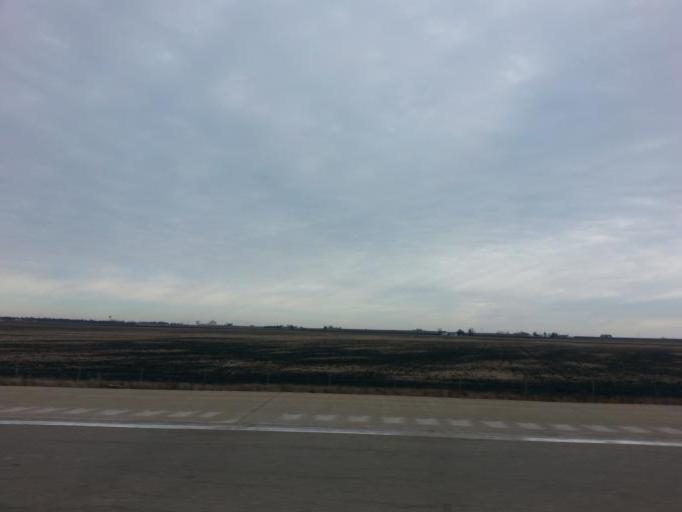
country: US
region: Illinois
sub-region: Woodford County
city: El Paso
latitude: 40.7116
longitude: -89.0305
